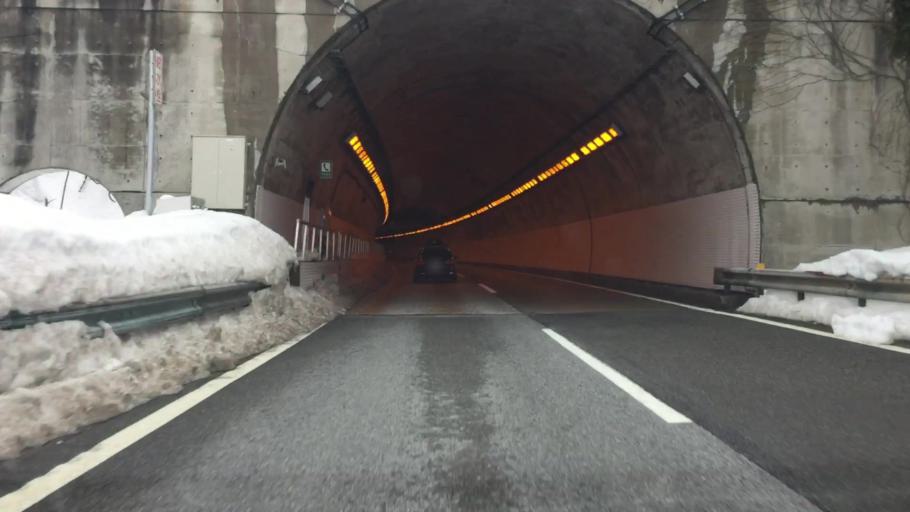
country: JP
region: Niigata
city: Shiozawa
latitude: 36.9759
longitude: 138.8095
